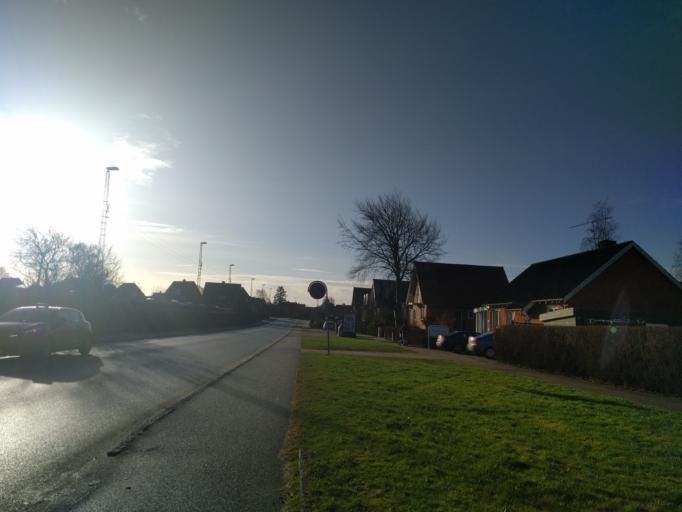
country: DK
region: Central Jutland
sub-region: Viborg Kommune
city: Viborg
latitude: 56.4620
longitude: 9.4166
